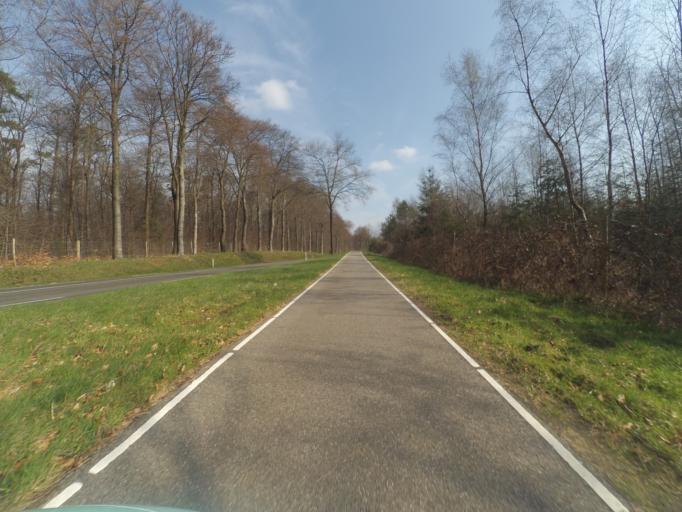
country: NL
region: Gelderland
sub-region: Gemeente Apeldoorn
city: Beekbergen
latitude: 52.1586
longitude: 5.8941
